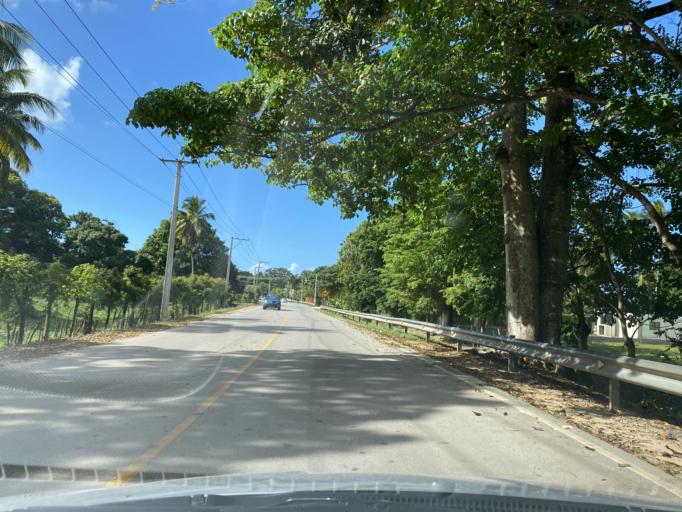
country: DO
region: Samana
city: Las Terrenas
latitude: 19.3065
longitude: -69.5508
